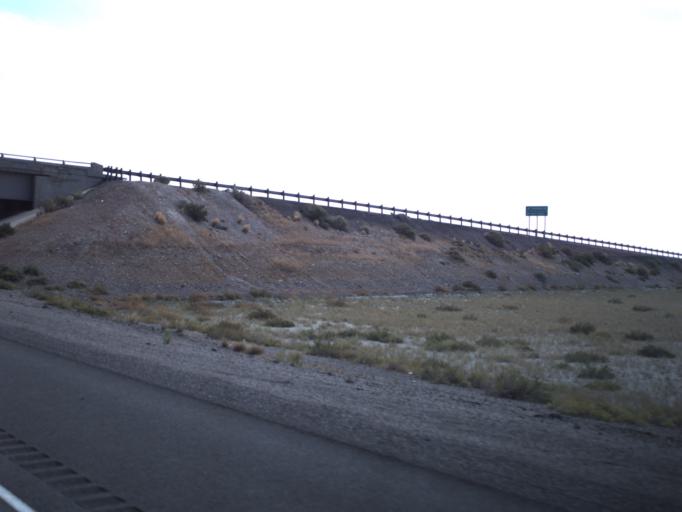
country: US
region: Utah
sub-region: Tooele County
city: Wendover
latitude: 40.7421
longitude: -113.9711
